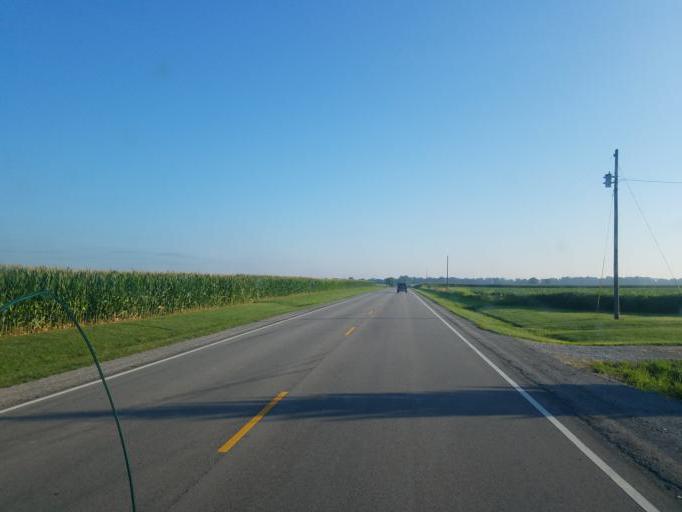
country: US
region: Illinois
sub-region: Bond County
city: Greenville
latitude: 38.8486
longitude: -89.3714
